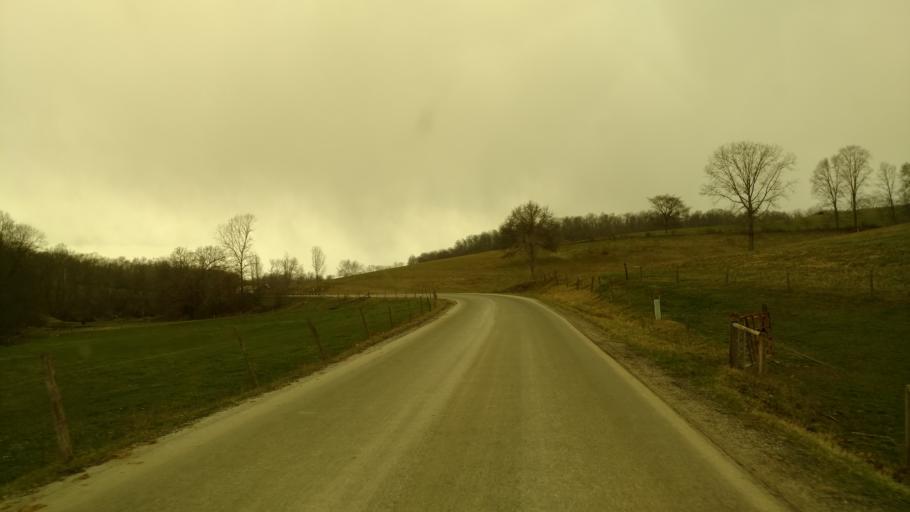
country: US
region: Ohio
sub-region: Tuscarawas County
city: Sugarcreek
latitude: 40.4465
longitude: -81.7893
